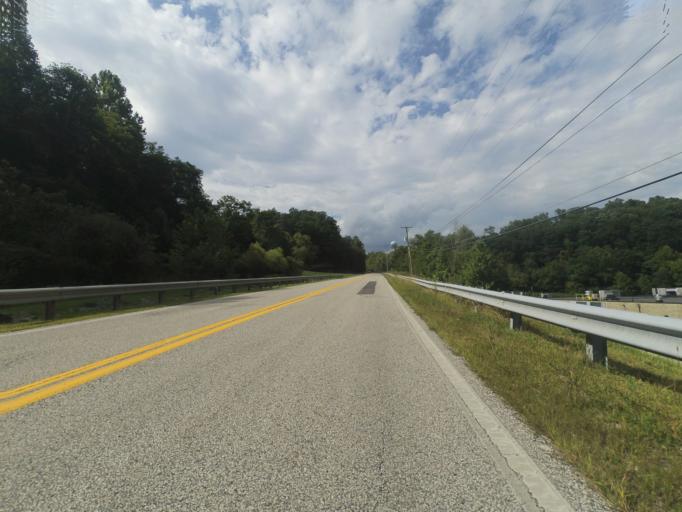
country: US
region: West Virginia
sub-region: Cabell County
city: Huntington
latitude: 38.3881
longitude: -82.4582
